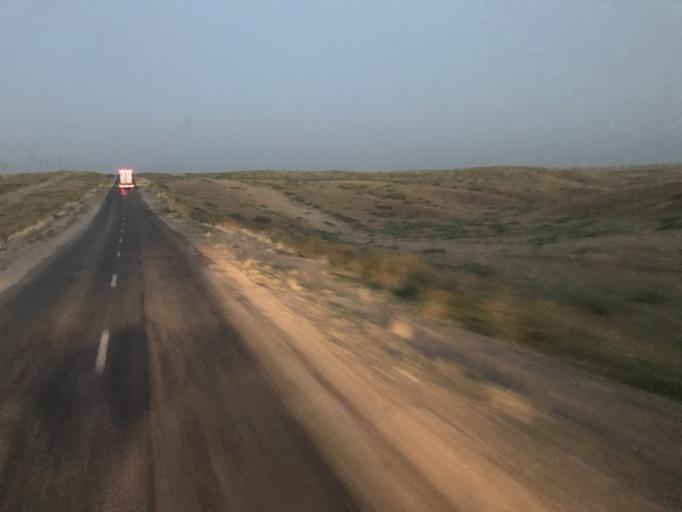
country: UZ
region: Toshkent
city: Chinoz
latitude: 41.1396
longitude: 68.7055
